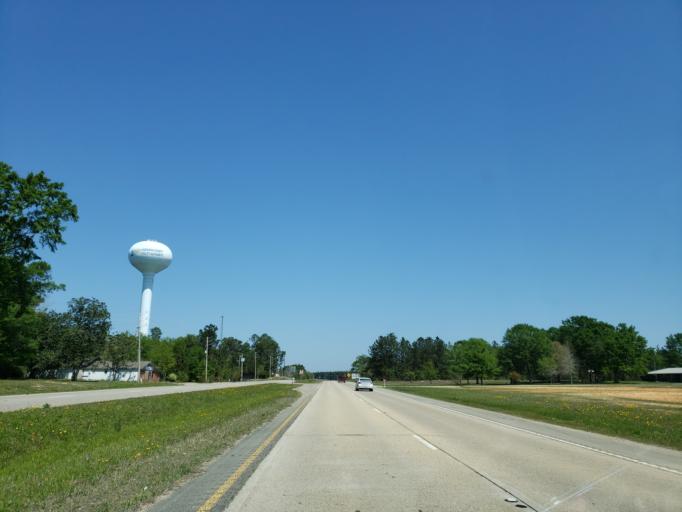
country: US
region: Mississippi
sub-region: Harrison County
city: Saucier
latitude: 30.5884
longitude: -89.1274
